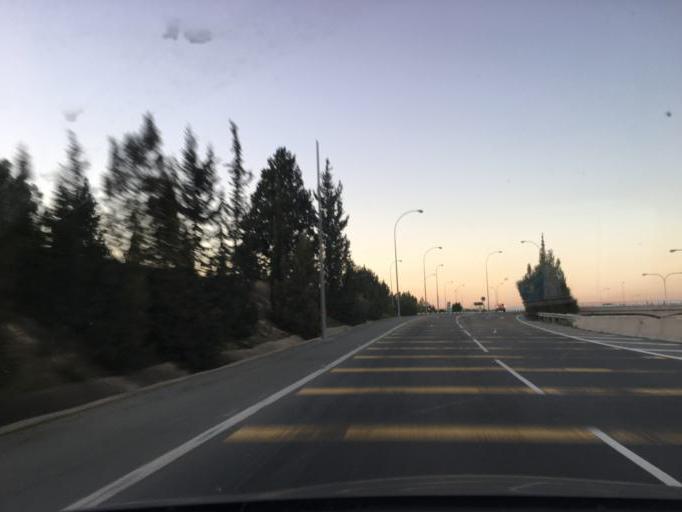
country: CY
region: Larnaka
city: Dhromolaxia
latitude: 34.9064
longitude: 33.5681
